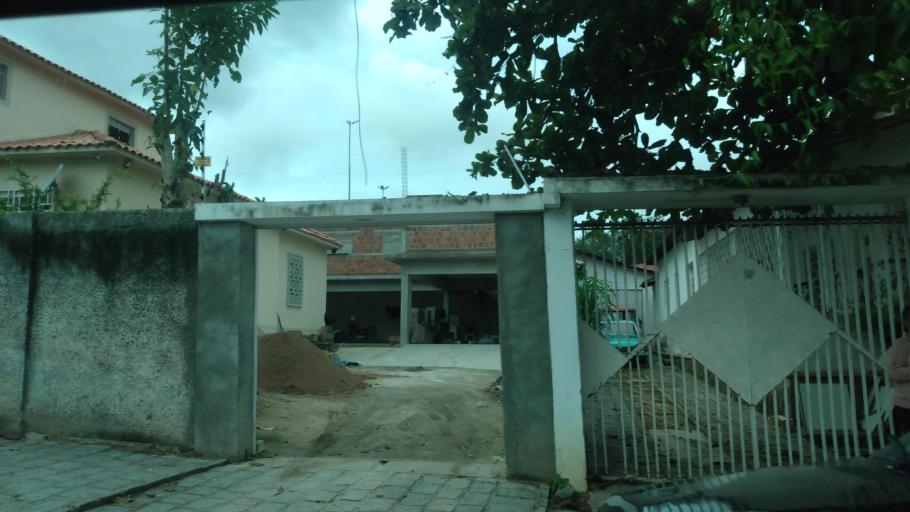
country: BR
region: Pernambuco
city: Garanhuns
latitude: -8.8888
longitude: -36.4892
